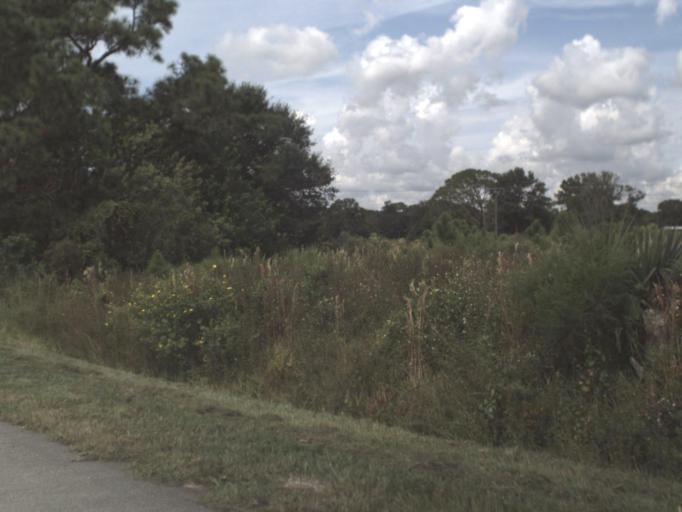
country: US
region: Florida
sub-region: Okeechobee County
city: Cypress Quarters
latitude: 27.2520
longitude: -80.7763
